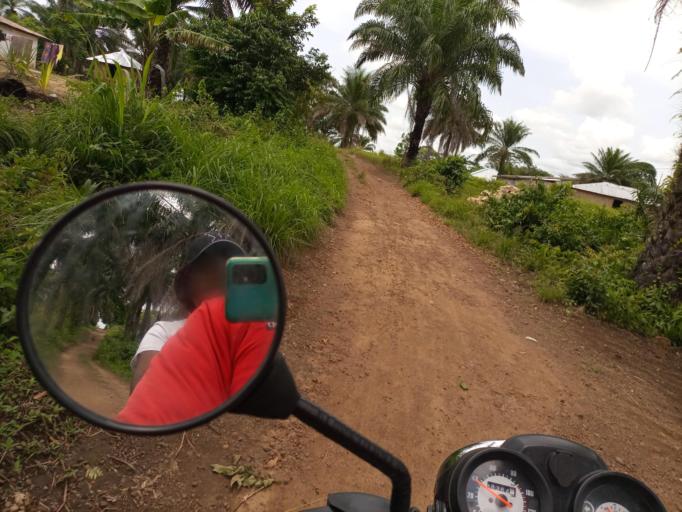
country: SL
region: Southern Province
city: Baoma
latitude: 7.9794
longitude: -11.7142
